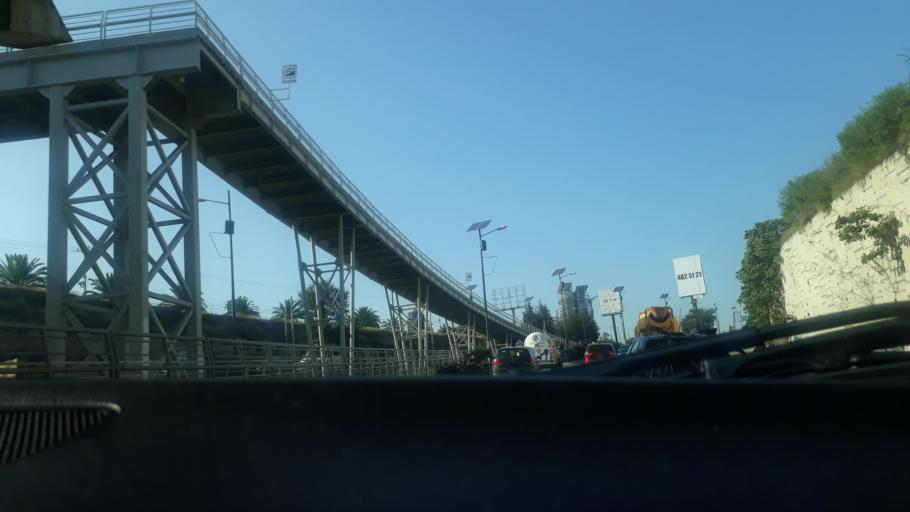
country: MX
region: Puebla
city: Tlazcalancingo
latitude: 19.0004
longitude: -98.2604
